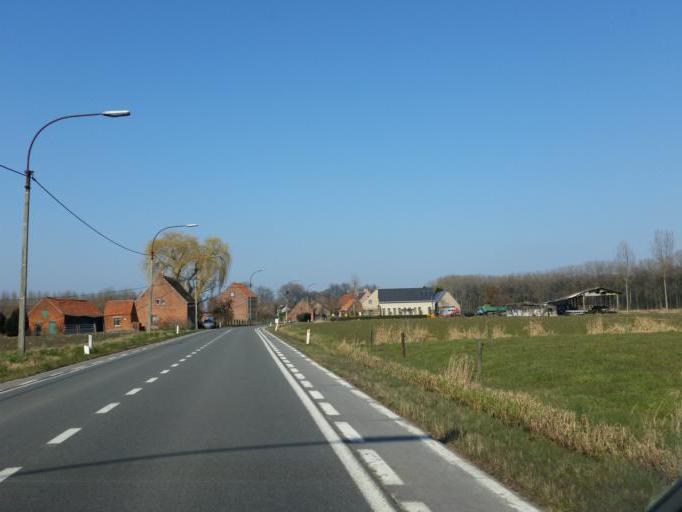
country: BE
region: Flanders
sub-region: Provincie Oost-Vlaanderen
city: Wachtebeke
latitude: 51.1425
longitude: 3.8662
